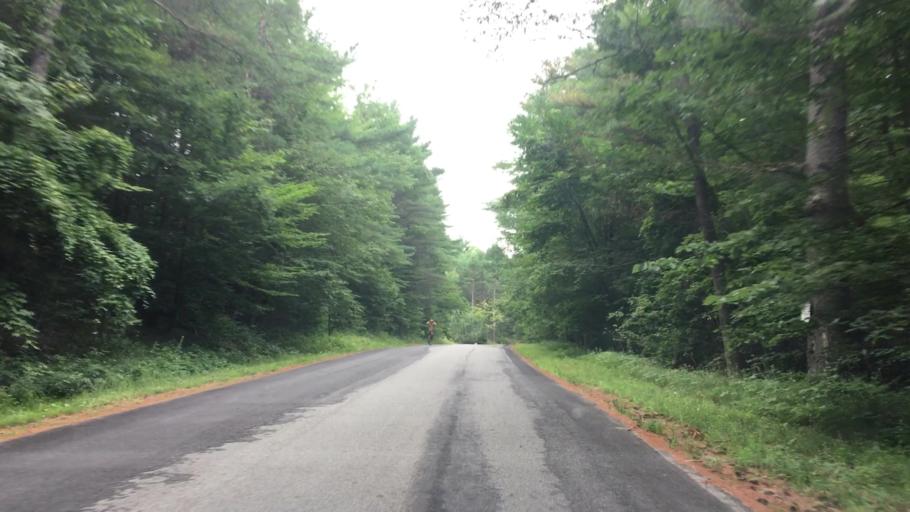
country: US
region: New York
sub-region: Essex County
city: Keeseville
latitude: 44.4622
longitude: -73.5747
